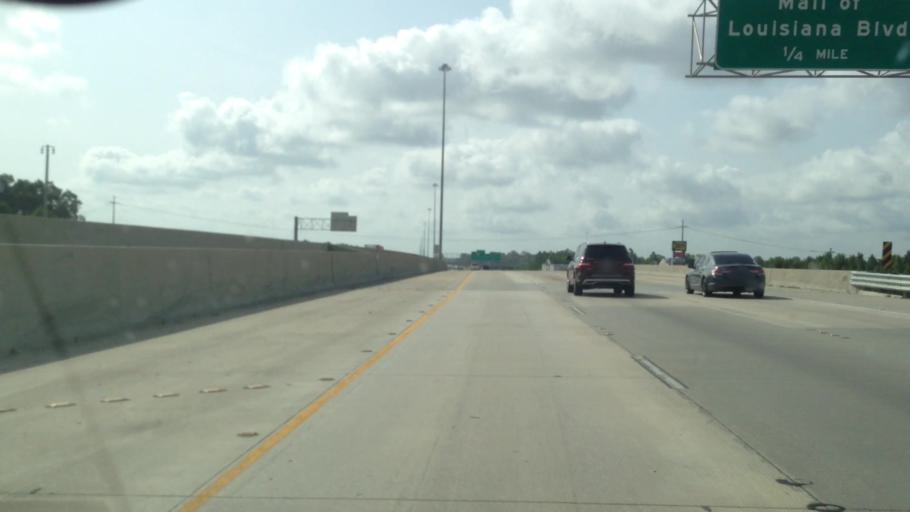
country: US
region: Louisiana
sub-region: East Baton Rouge Parish
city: Inniswold
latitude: 30.3955
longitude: -91.0865
